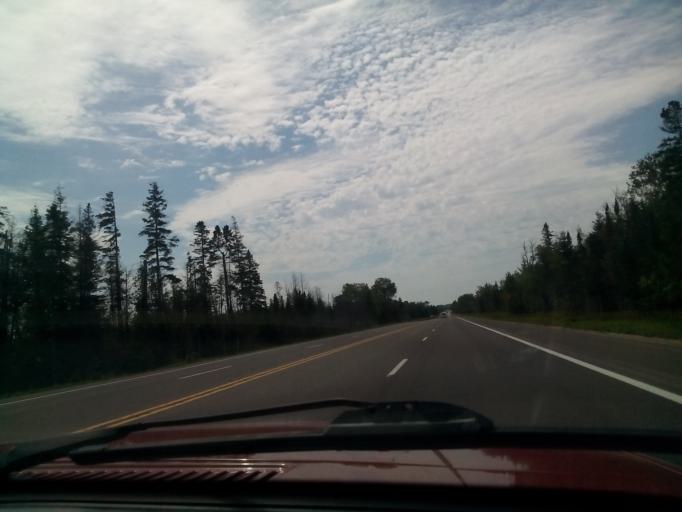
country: US
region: Michigan
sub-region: Schoolcraft County
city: Manistique
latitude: 46.0087
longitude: -85.9967
